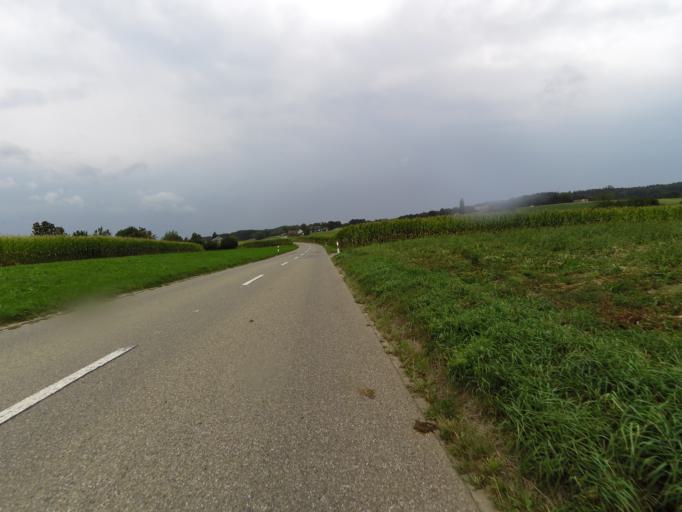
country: CH
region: Thurgau
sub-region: Frauenfeld District
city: Homburg
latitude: 47.6375
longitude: 9.0497
